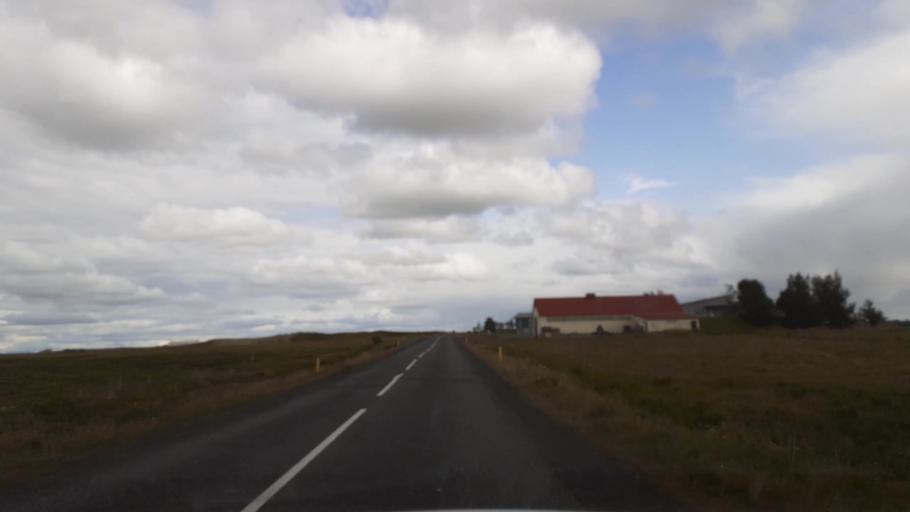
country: IS
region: South
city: Vestmannaeyjar
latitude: 63.8298
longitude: -20.4239
